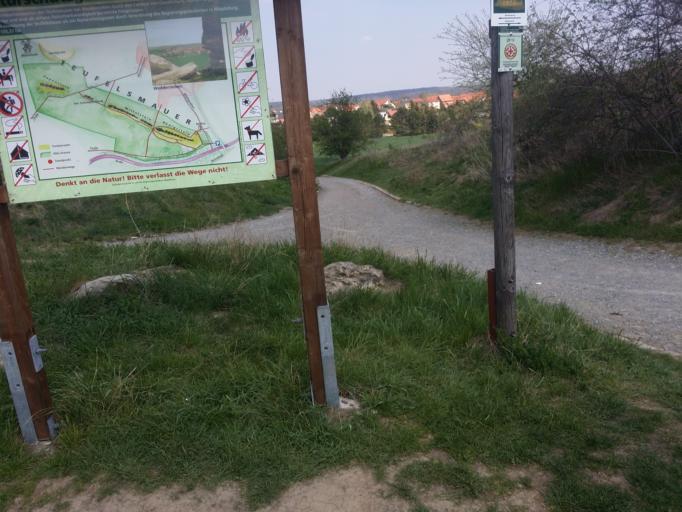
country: DE
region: Saxony-Anhalt
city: Weddersleben
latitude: 51.7590
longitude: 11.0794
